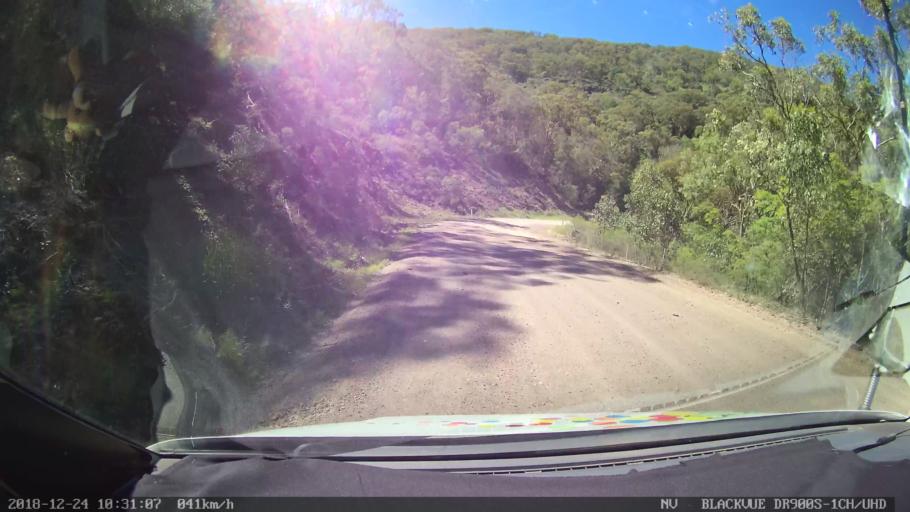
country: AU
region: New South Wales
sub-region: Upper Hunter Shire
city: Merriwa
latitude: -31.8383
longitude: 150.5230
